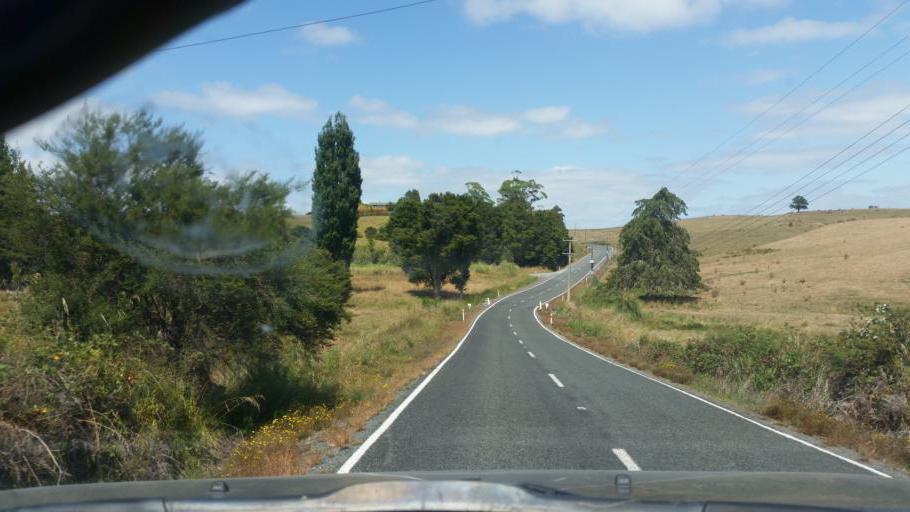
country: NZ
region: Northland
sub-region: Whangarei
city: Ruakaka
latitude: -36.0148
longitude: 174.2893
